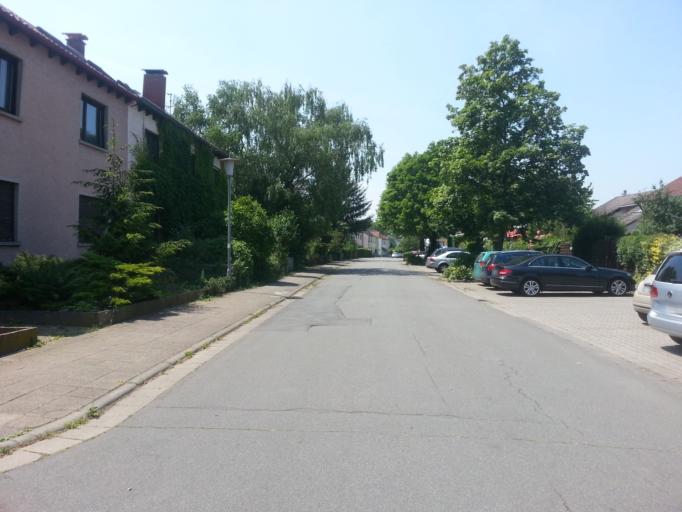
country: DE
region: Baden-Wuerttemberg
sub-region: Karlsruhe Region
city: Ladenburg
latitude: 49.4736
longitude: 8.6211
